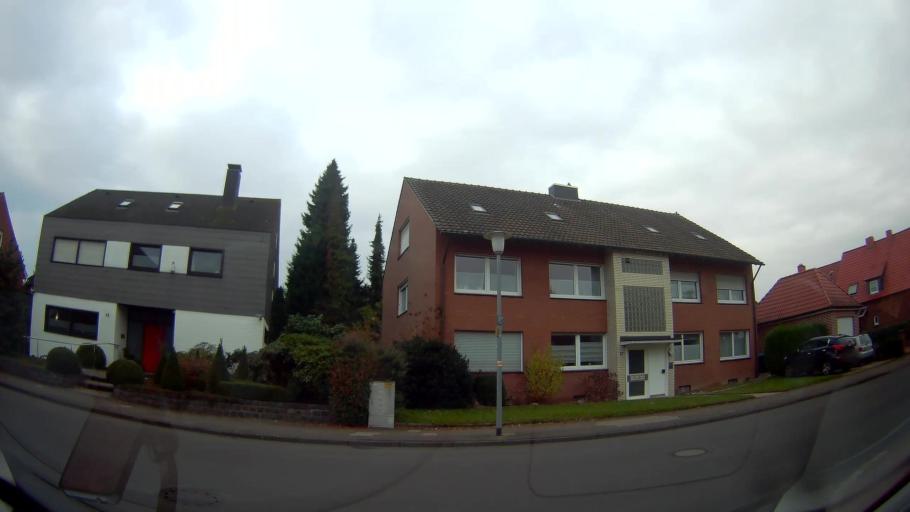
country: DE
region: North Rhine-Westphalia
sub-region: Regierungsbezirk Munster
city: Haltern
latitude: 51.7486
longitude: 7.1881
